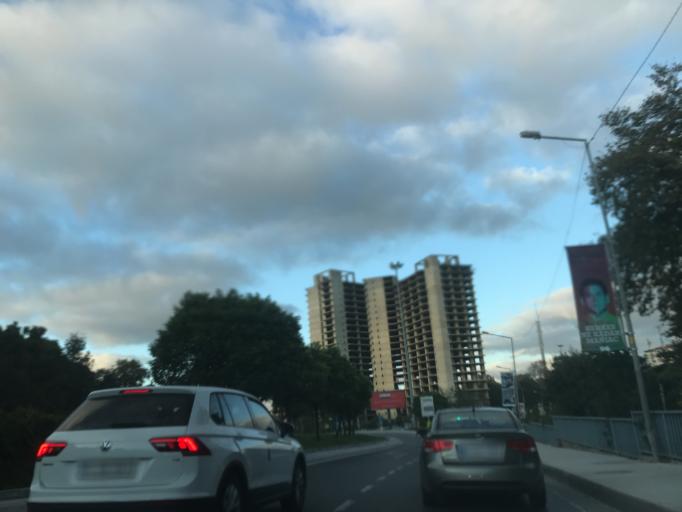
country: TR
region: Istanbul
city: Sisli
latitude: 41.1389
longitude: 29.0271
